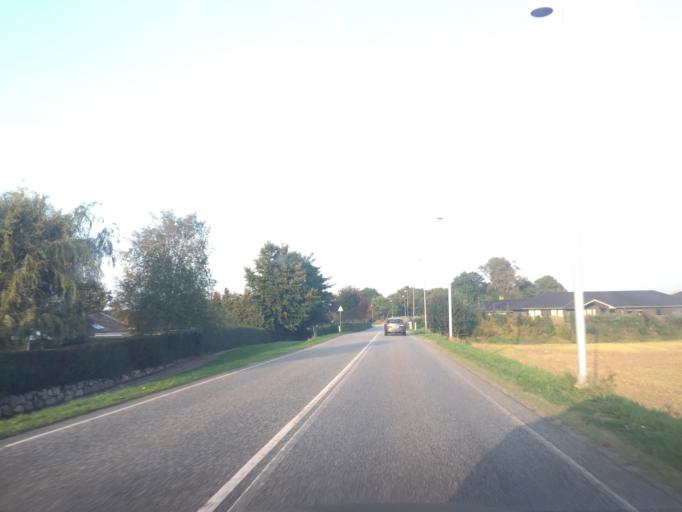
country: DK
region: Zealand
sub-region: Lejre Kommune
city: Kirke Hvalso
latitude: 55.5864
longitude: 11.8579
